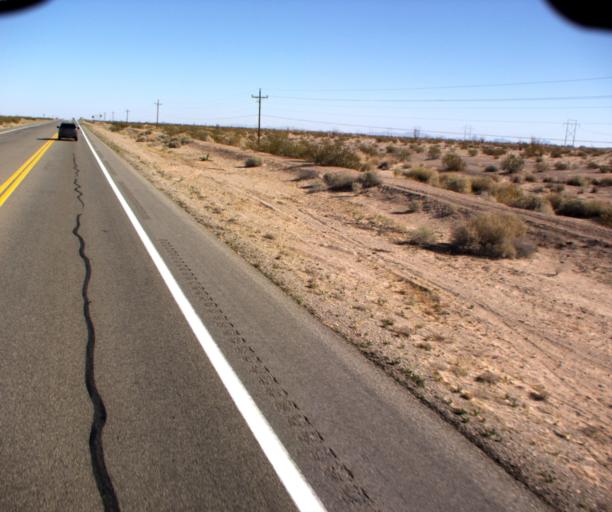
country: US
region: Arizona
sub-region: Yuma County
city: Fortuna Foothills
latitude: 32.8107
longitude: -114.3797
